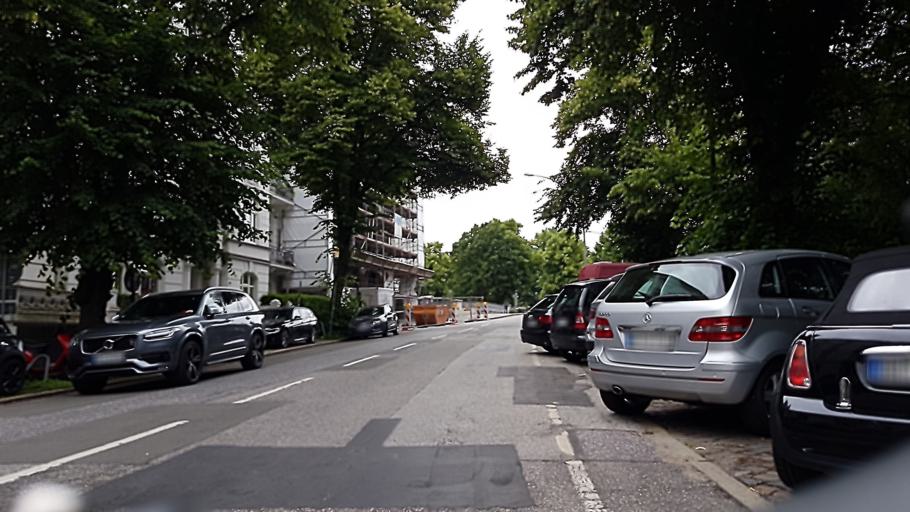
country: DE
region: Hamburg
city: Hamburg-Nord
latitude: 53.5839
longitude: 9.9938
